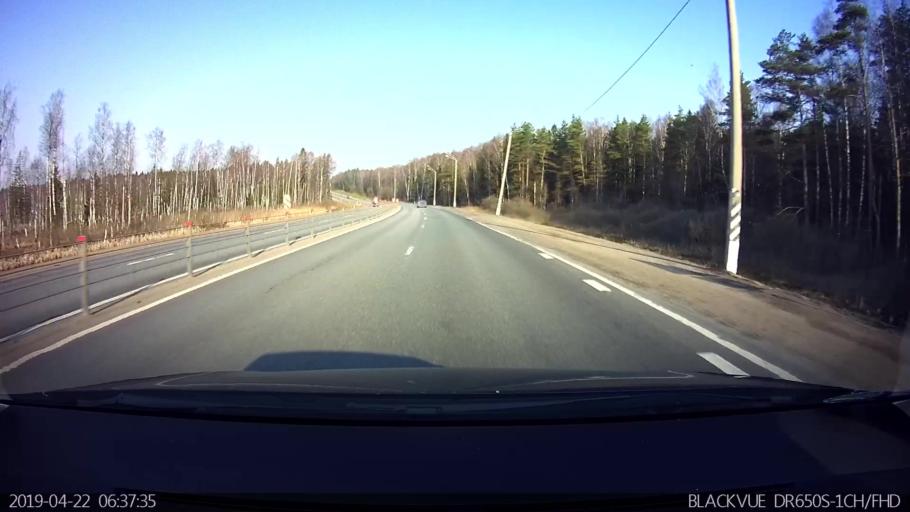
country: RU
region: Moskovskaya
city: Uvarovka
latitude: 55.4911
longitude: 35.4014
